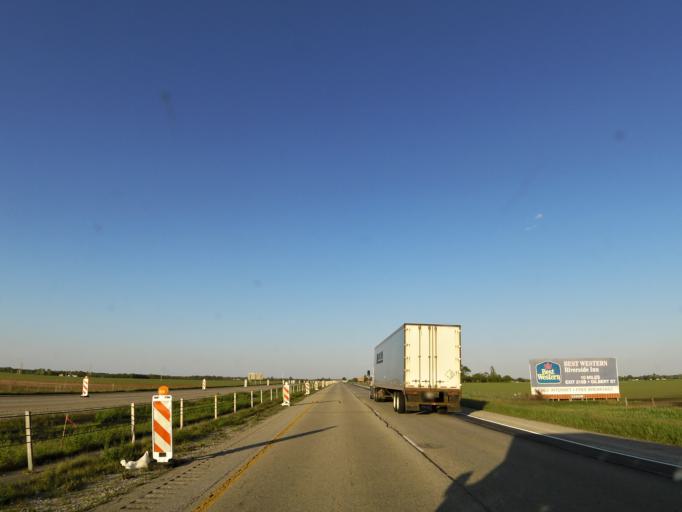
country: US
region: Illinois
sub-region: Vermilion County
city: Oakwood
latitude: 40.1258
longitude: -87.8031
